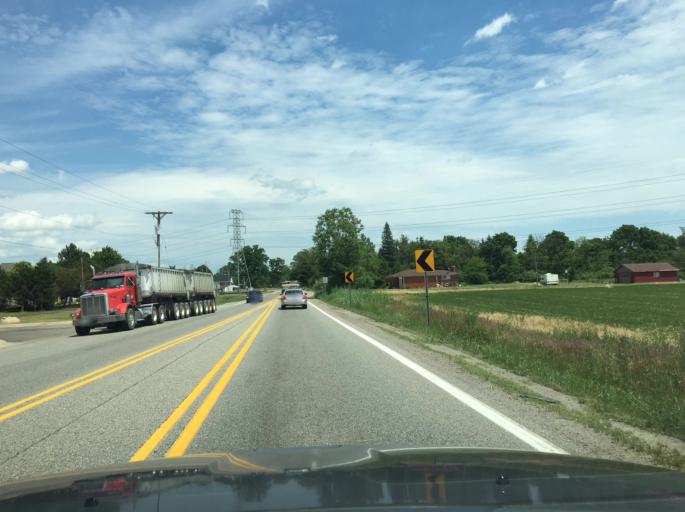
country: US
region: Michigan
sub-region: Macomb County
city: Shelby
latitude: 42.7142
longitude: -83.0147
